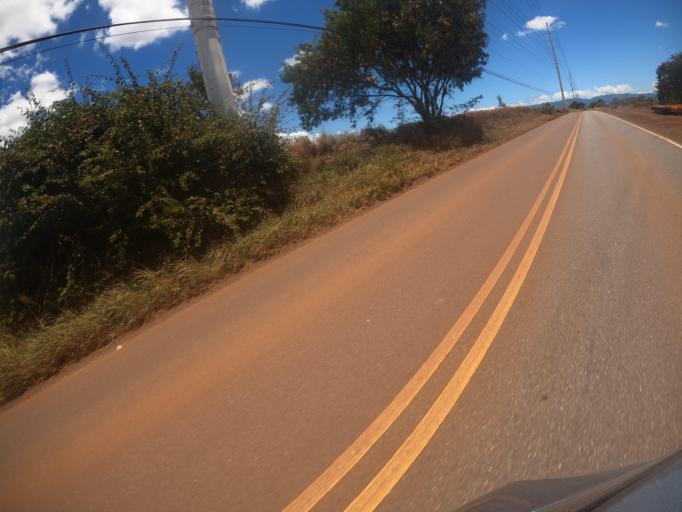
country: US
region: Hawaii
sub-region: Honolulu County
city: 'Ewa Villages
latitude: 21.3677
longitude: -158.0511
